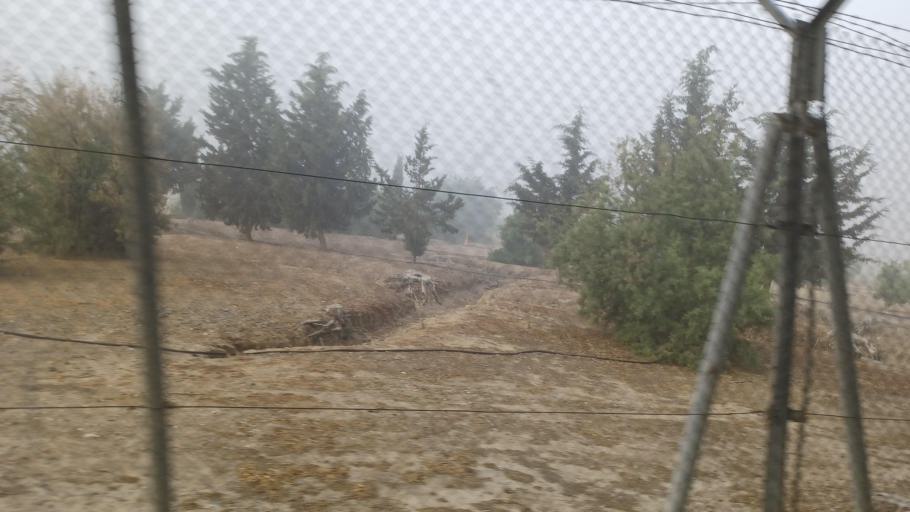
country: CY
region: Ammochostos
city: Acheritou
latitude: 35.0917
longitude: 33.8791
